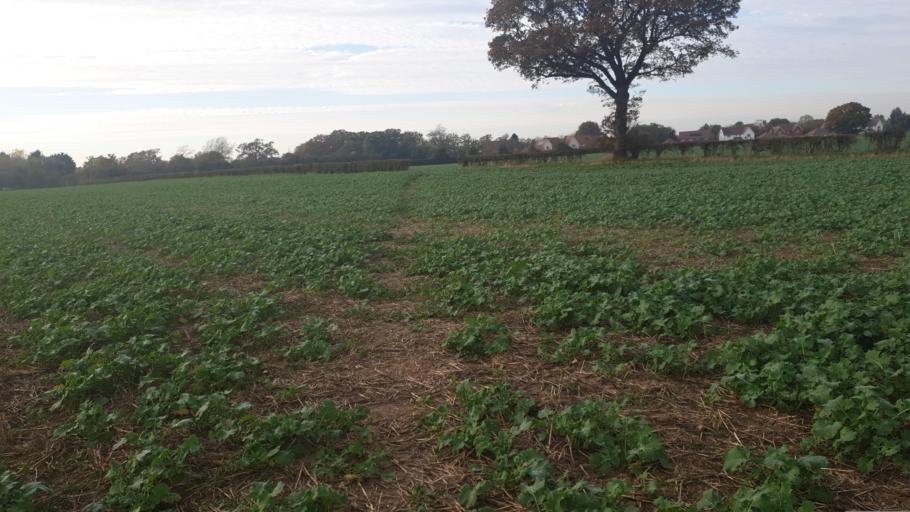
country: GB
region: England
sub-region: Essex
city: Great Bentley
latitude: 51.8877
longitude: 1.1148
